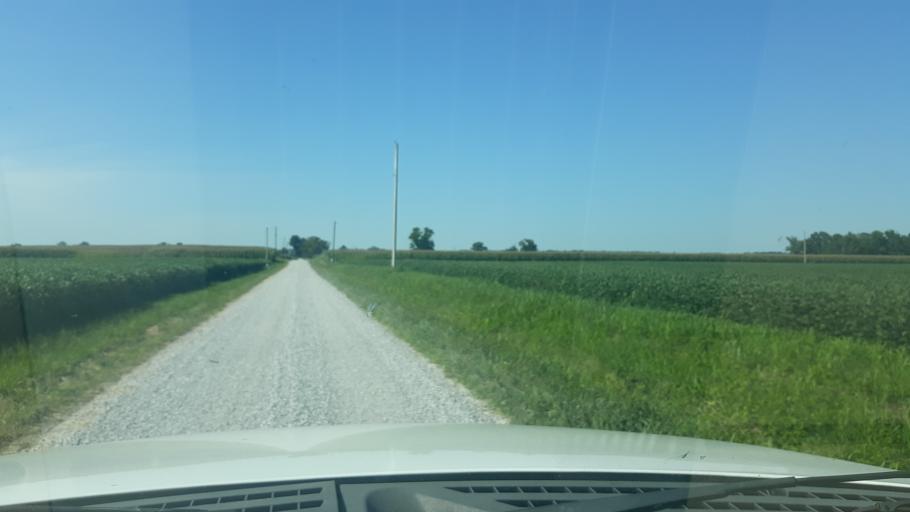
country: US
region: Illinois
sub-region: Saline County
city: Eldorado
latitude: 37.8544
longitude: -88.4850
